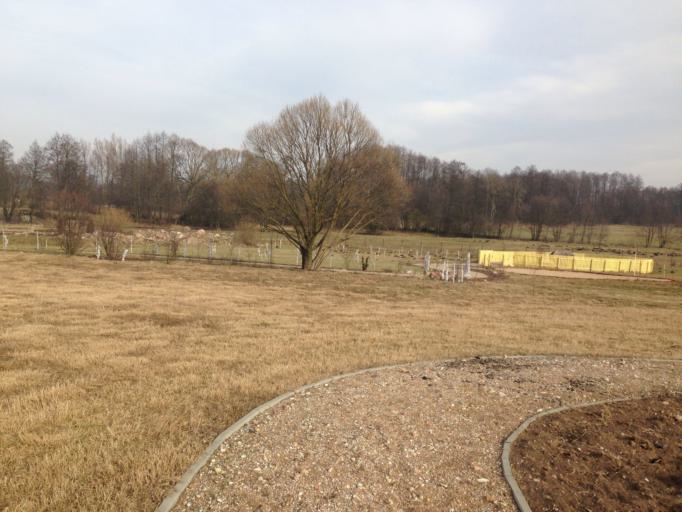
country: PL
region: Warmian-Masurian Voivodeship
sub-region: Powiat nidzicki
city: Nidzica
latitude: 53.3034
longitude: 20.4214
